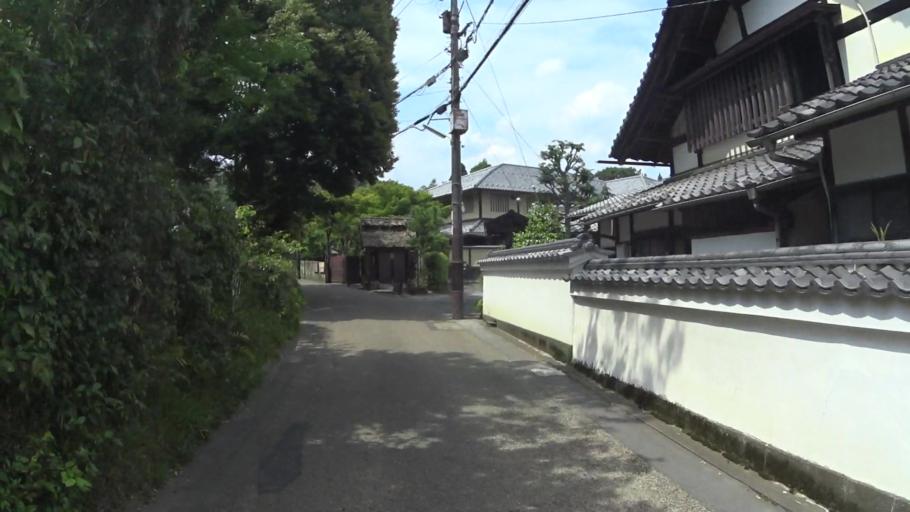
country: JP
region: Kyoto
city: Muko
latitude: 35.0237
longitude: 135.6686
